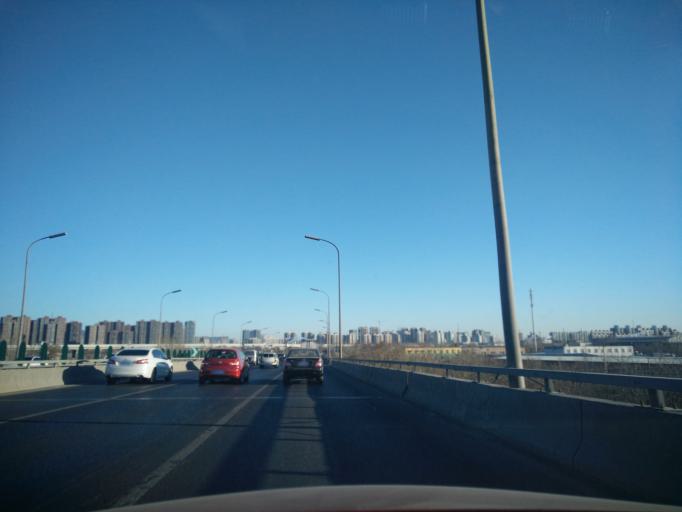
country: CN
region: Beijing
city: Lugu
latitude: 39.8810
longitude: 116.2025
